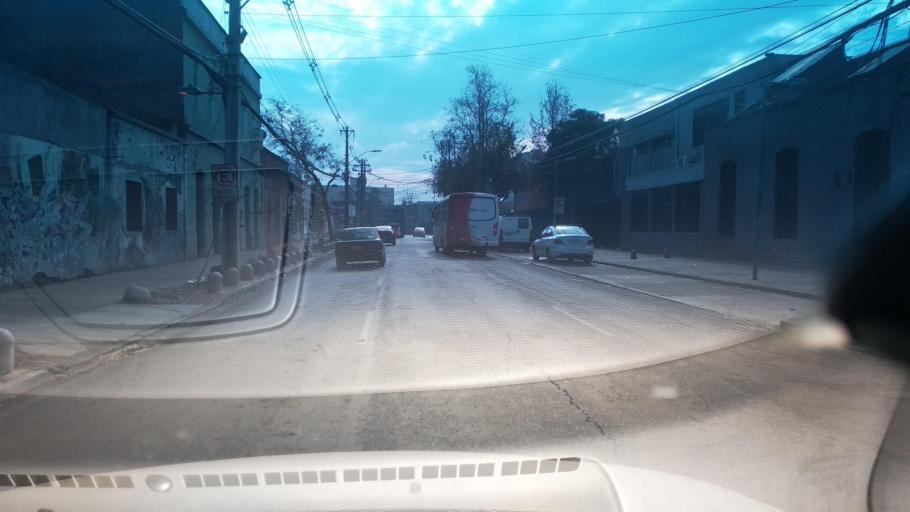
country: CL
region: Santiago Metropolitan
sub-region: Provincia de Santiago
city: Santiago
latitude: -33.4566
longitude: -70.6840
